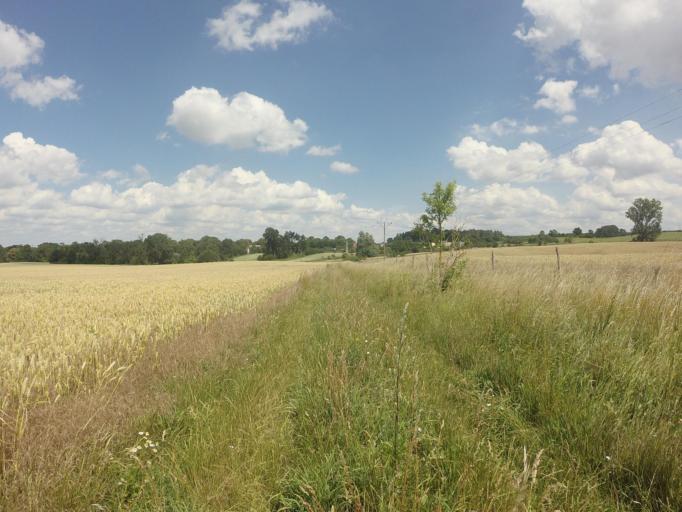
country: PL
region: West Pomeranian Voivodeship
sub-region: Powiat choszczenski
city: Recz
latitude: 53.2100
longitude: 15.4937
